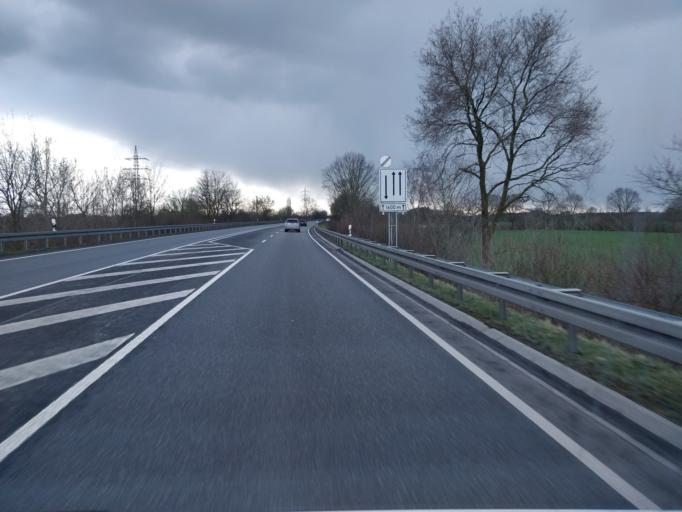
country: DE
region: North Rhine-Westphalia
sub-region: Regierungsbezirk Dusseldorf
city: Bocholt
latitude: 51.8117
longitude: 6.5933
